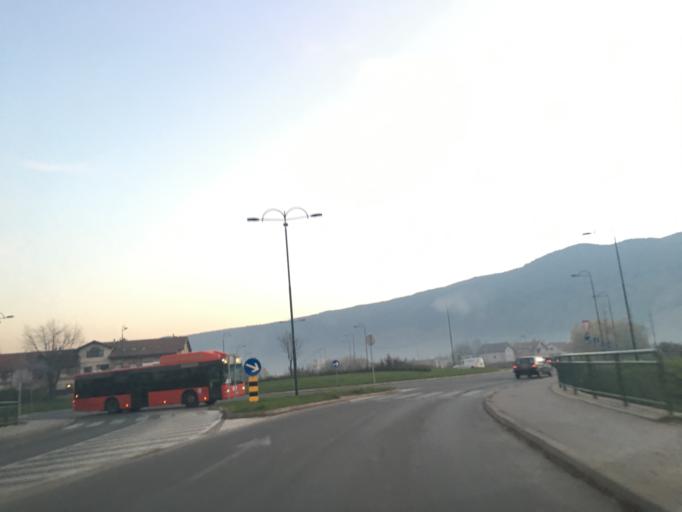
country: BA
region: Federation of Bosnia and Herzegovina
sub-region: Kanton Sarajevo
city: Sarajevo
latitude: 43.8202
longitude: 18.3075
